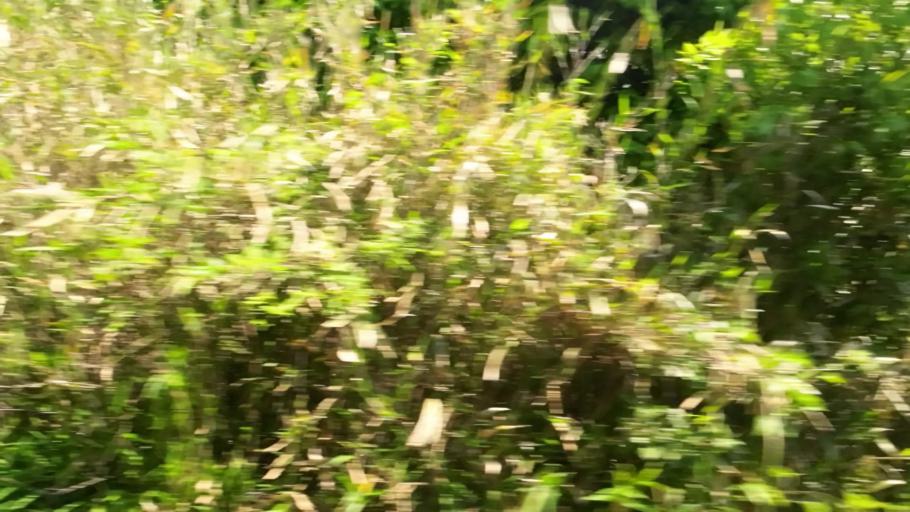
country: JP
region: Ehime
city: Hojo
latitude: 34.0616
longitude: 132.9054
